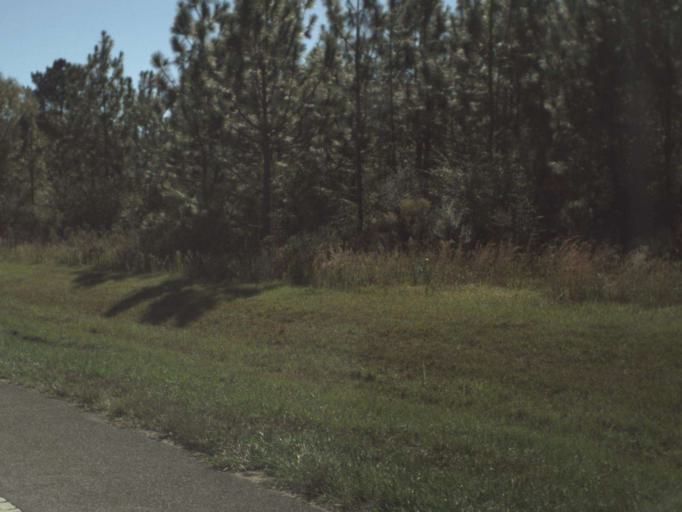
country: US
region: Florida
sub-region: Okaloosa County
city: Crestview
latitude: 30.8116
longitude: -86.7092
